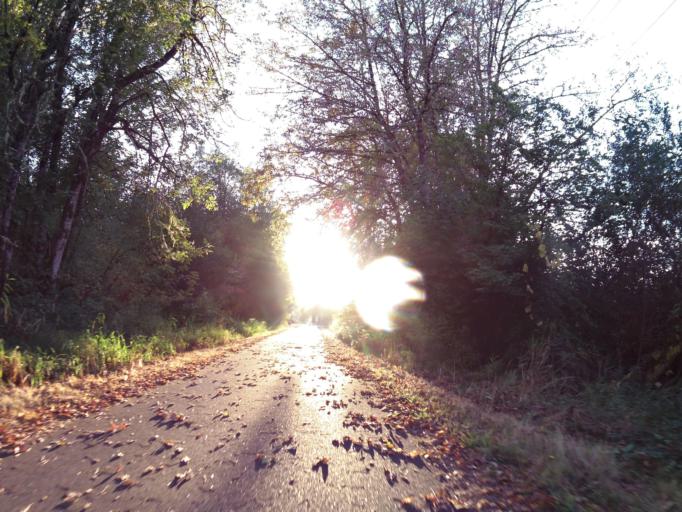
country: US
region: Washington
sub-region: Thurston County
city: Tenino
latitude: 46.8575
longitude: -122.8222
